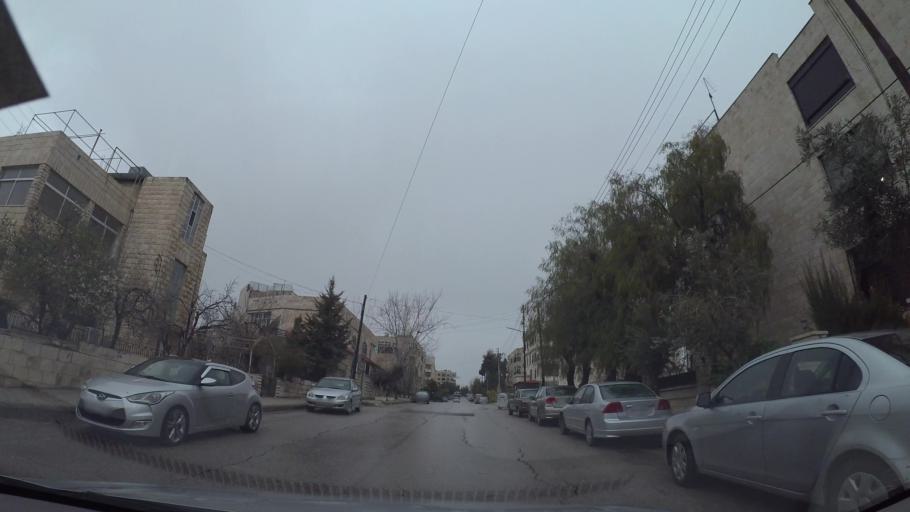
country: JO
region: Amman
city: Al Jubayhah
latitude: 32.0263
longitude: 35.8538
